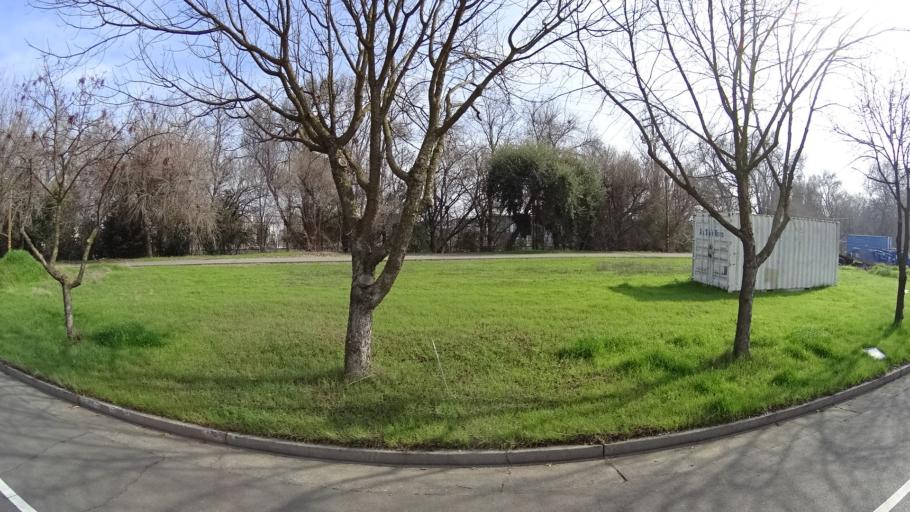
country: US
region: California
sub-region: Yolo County
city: Davis
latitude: 38.5627
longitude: -121.7444
